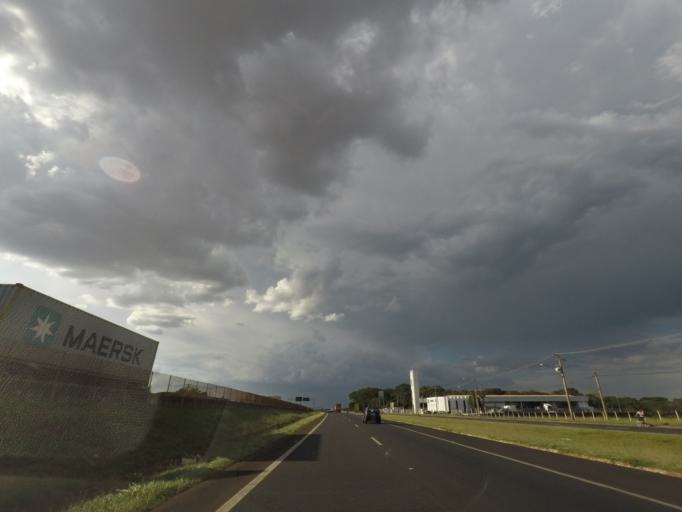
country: BR
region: Sao Paulo
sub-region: Ribeirao Preto
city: Ribeirao Preto
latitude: -21.1430
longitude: -47.7602
